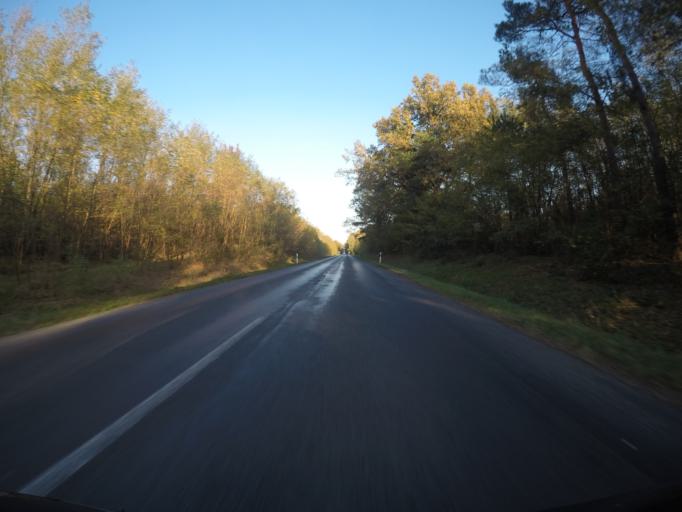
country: HU
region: Somogy
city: Barcs
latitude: 45.9749
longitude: 17.5502
